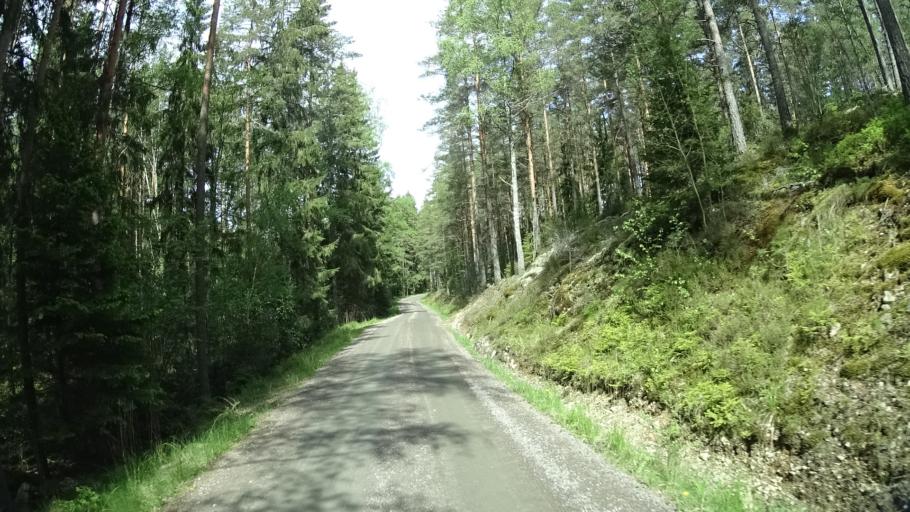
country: SE
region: OEstergoetland
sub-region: Finspangs Kommun
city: Finspang
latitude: 58.7600
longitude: 15.8353
